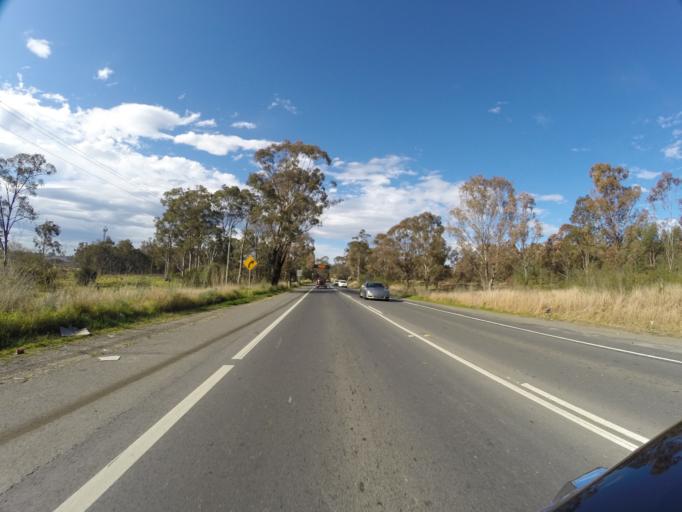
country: AU
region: New South Wales
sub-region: Fairfield
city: Cecil Park
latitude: -33.8750
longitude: 150.8372
